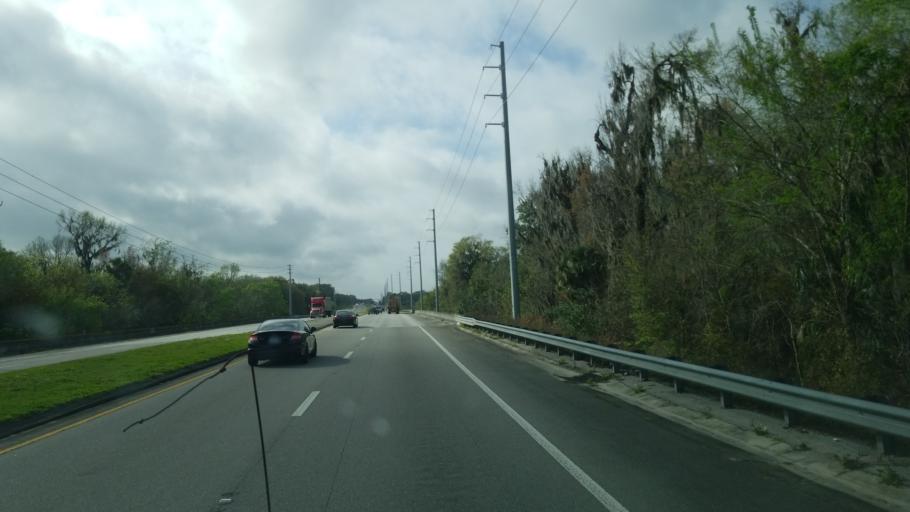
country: US
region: Florida
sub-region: Polk County
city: Willow Oak
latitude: 27.9605
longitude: -82.0556
